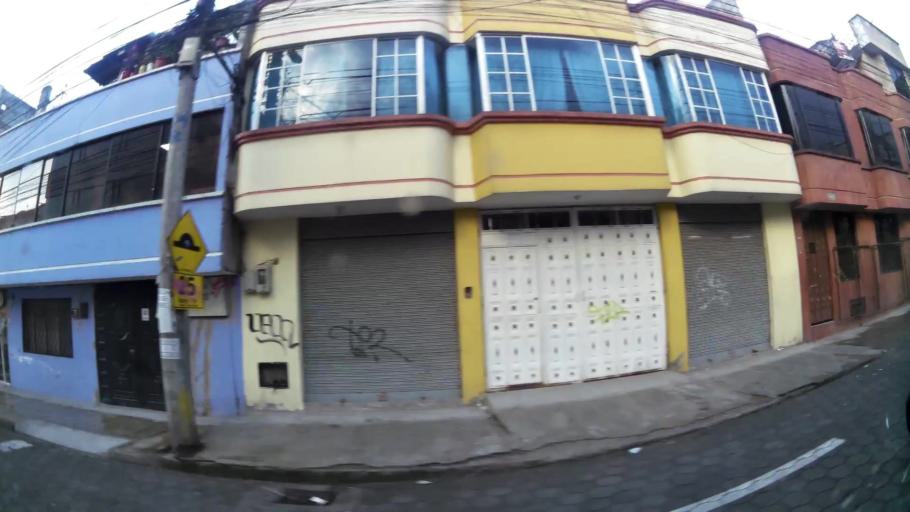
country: EC
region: Pichincha
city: Quito
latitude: -0.3050
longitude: -78.5411
